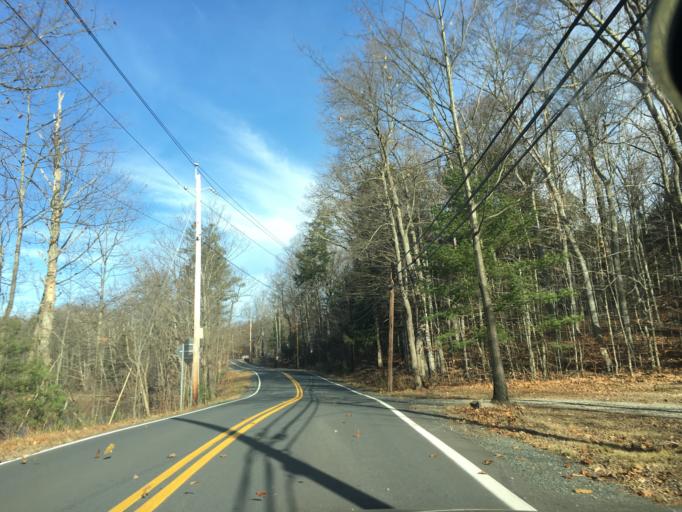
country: US
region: New York
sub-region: Rensselaer County
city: Averill Park
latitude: 42.6220
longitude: -73.5661
